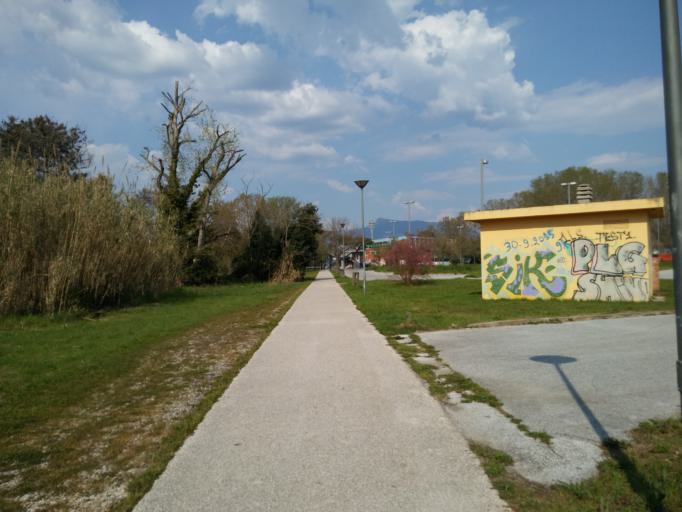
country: IT
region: Tuscany
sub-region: Provincia di Lucca
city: Viareggio
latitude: 43.8567
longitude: 10.2463
